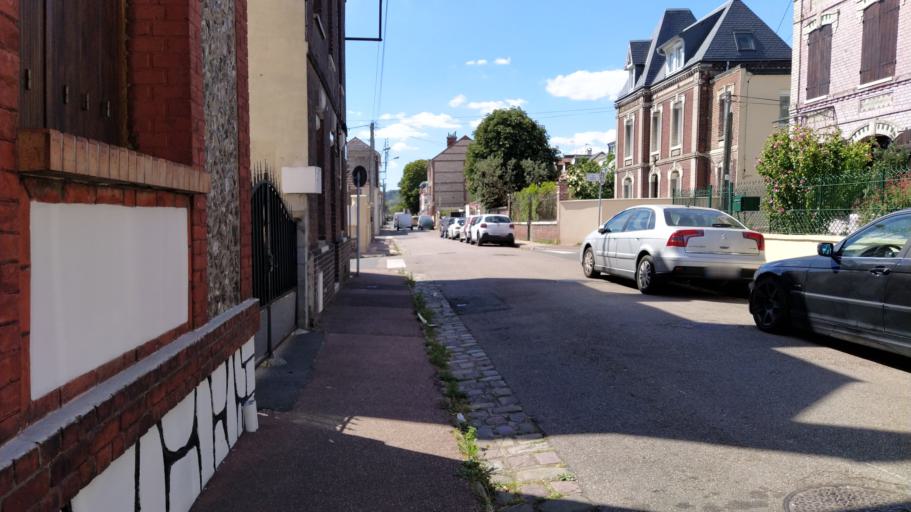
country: FR
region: Haute-Normandie
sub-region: Departement de la Seine-Maritime
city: Le Petit-Quevilly
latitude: 49.4317
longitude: 1.0651
